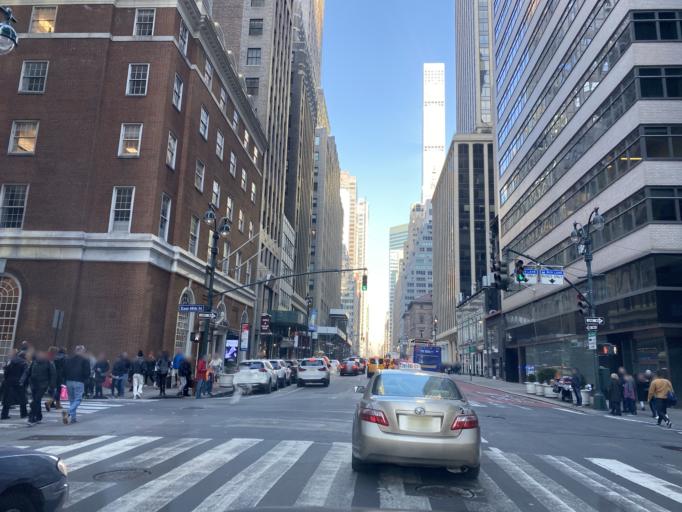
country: US
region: New York
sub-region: New York County
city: Manhattan
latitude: 40.7565
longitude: -73.9766
